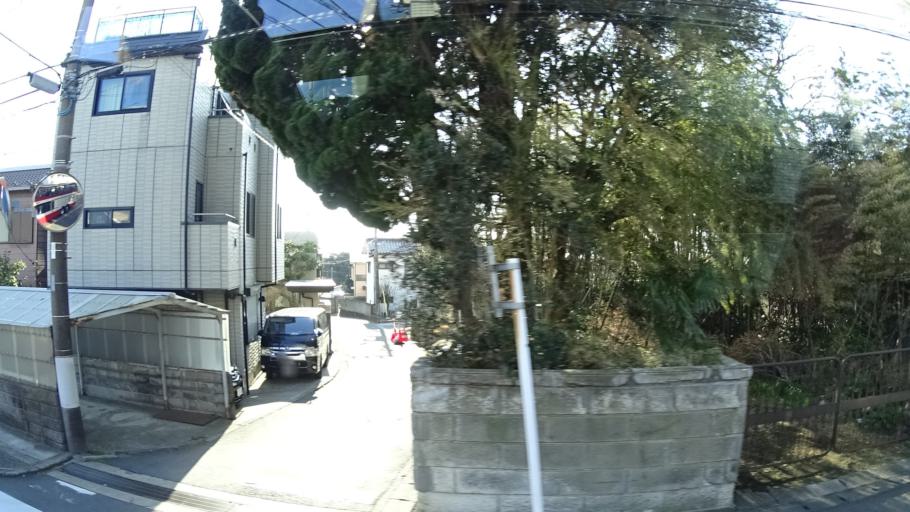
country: JP
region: Kanagawa
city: Miura
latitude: 35.1539
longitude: 139.6304
